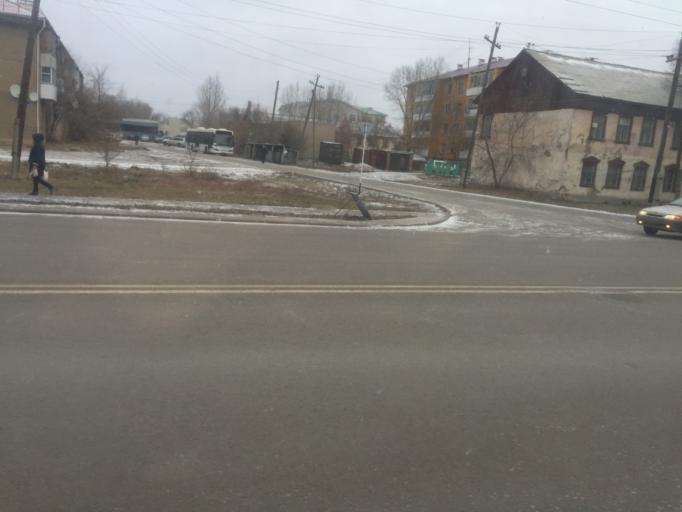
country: KZ
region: Astana Qalasy
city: Astana
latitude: 51.1990
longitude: 71.3913
